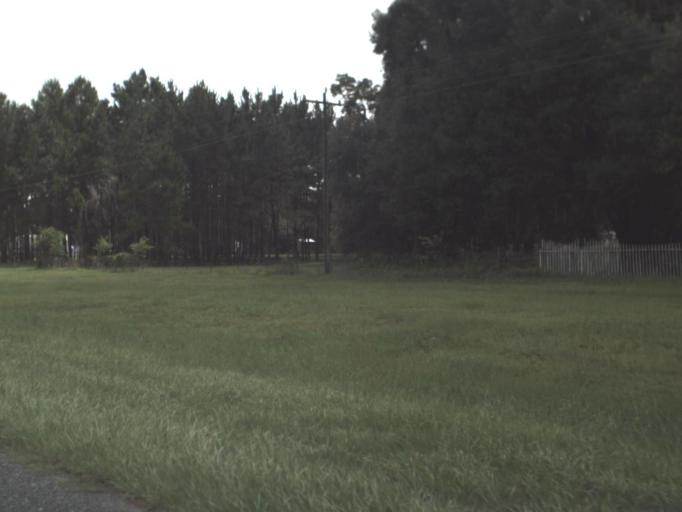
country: US
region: Florida
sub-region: Alachua County
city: High Springs
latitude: 29.9432
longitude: -82.6070
